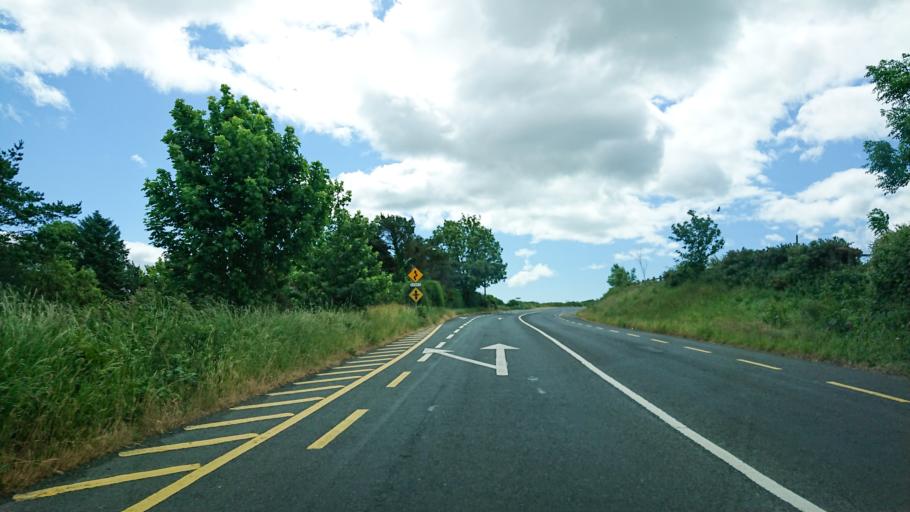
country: IE
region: Munster
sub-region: Waterford
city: Tra Mhor
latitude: 52.2142
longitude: -7.1950
